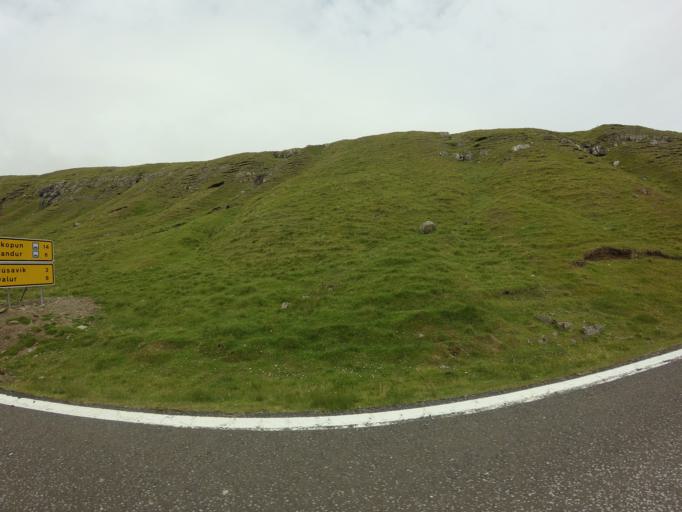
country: FO
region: Sandoy
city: Sandur
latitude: 61.8235
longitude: -6.7233
